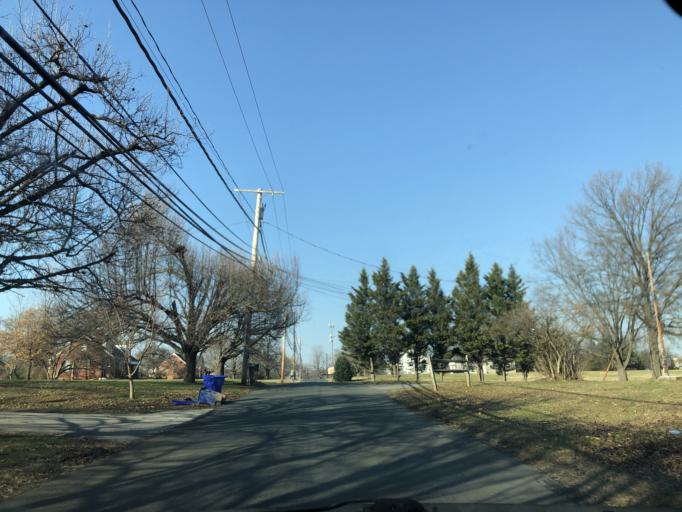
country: US
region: Maryland
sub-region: Montgomery County
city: Burtonsville
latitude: 39.1060
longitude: -76.9343
